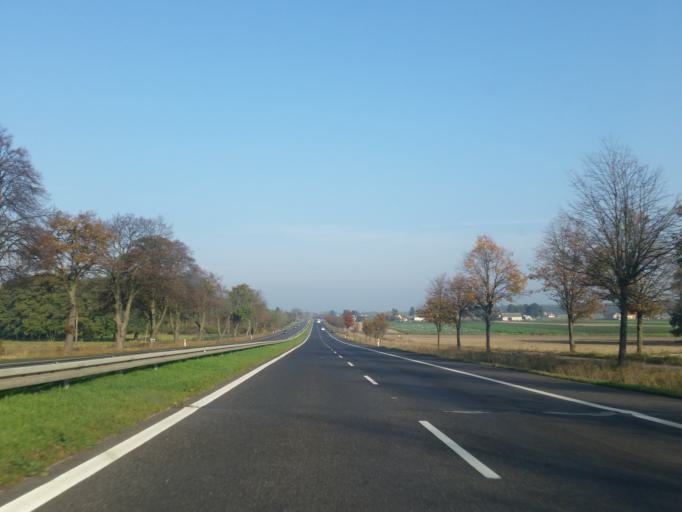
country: PL
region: Masovian Voivodeship
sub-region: Powiat plonski
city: Zaluski
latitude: 52.4914
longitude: 20.5455
